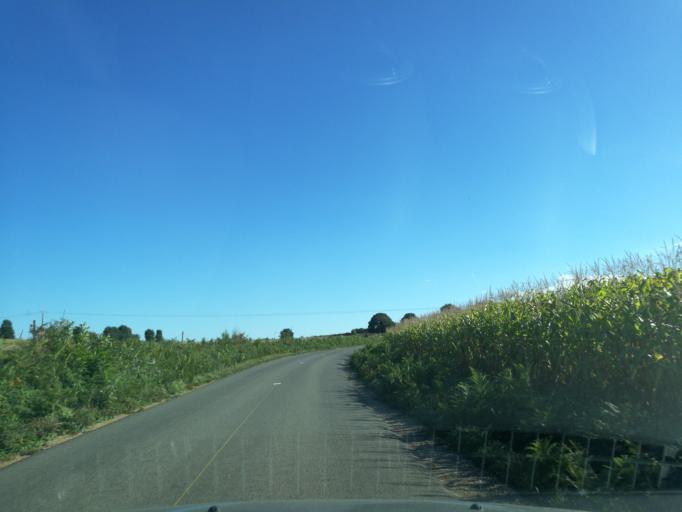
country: FR
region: Brittany
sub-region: Departement d'Ille-et-Vilaine
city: Montauban-de-Bretagne
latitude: 48.1781
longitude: -2.0399
